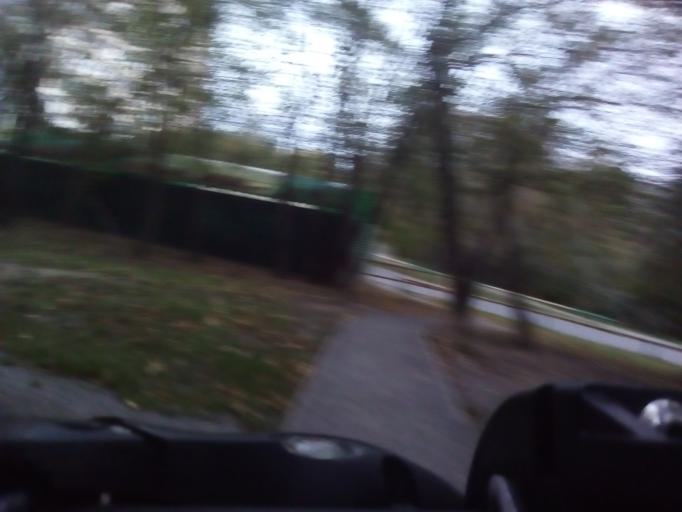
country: RU
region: Moscow
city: Sviblovo
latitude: 55.8558
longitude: 37.6386
